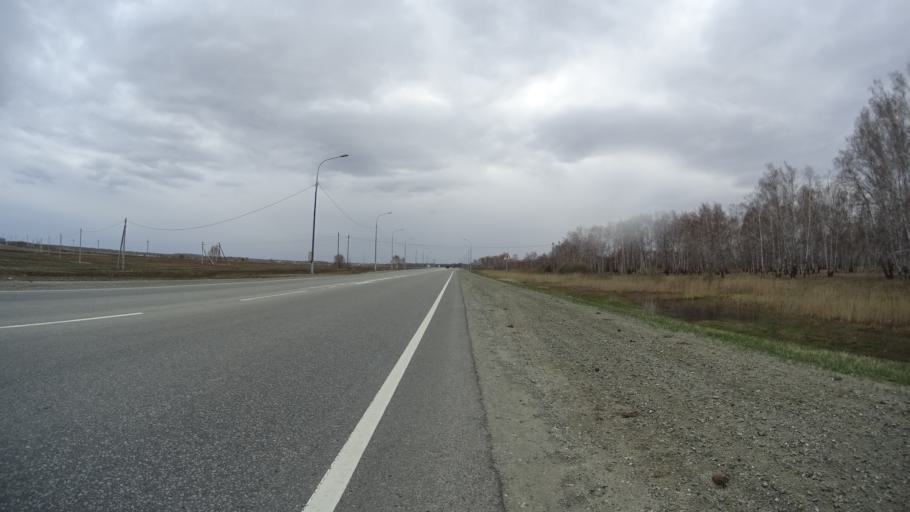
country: RU
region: Chelyabinsk
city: Krasnogorskiy
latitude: 54.6862
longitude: 61.2477
